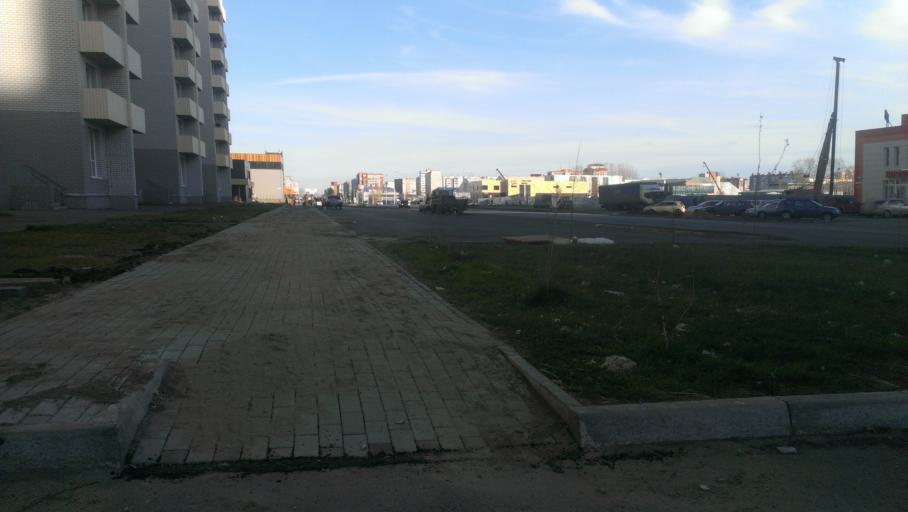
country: RU
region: Altai Krai
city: Novosilikatnyy
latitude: 53.3375
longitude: 83.6574
